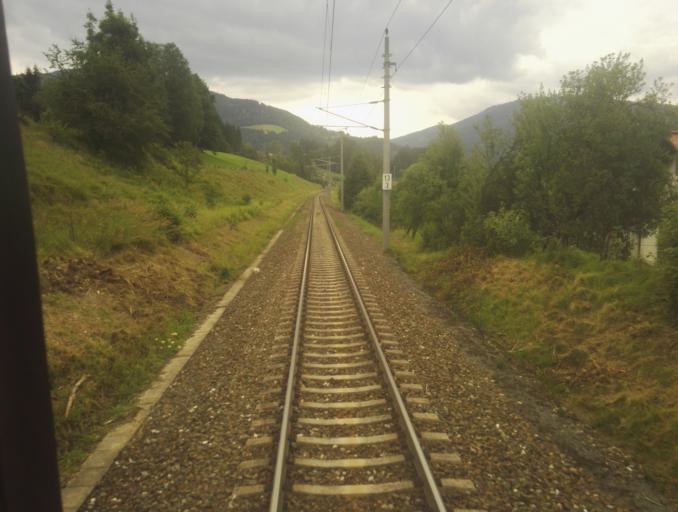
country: AT
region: Salzburg
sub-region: Politischer Bezirk Sankt Johann im Pongau
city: Eben im Pongau
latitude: 47.4218
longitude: 13.3587
